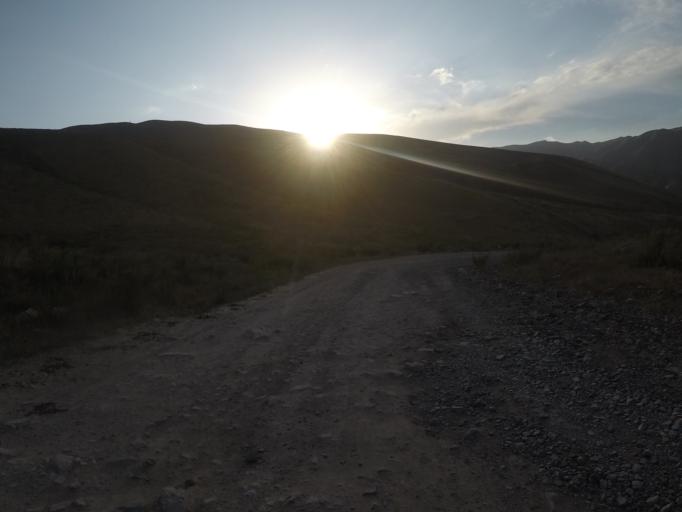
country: KG
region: Chuy
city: Bishkek
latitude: 42.6588
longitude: 74.6507
